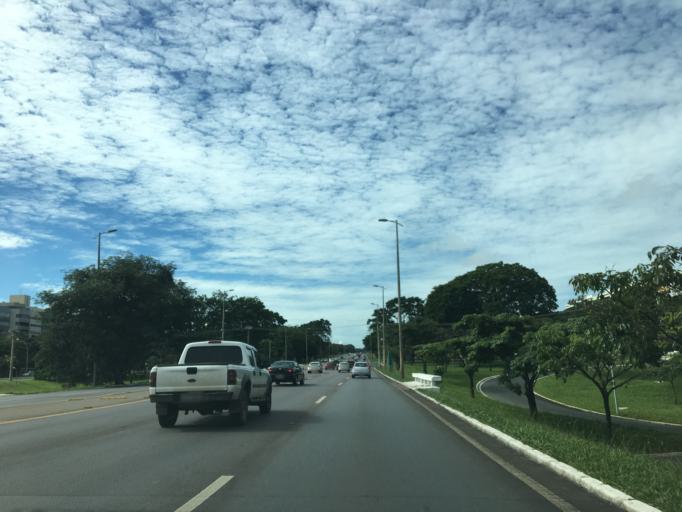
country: BR
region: Federal District
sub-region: Brasilia
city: Brasilia
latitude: -15.7516
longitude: -47.8876
